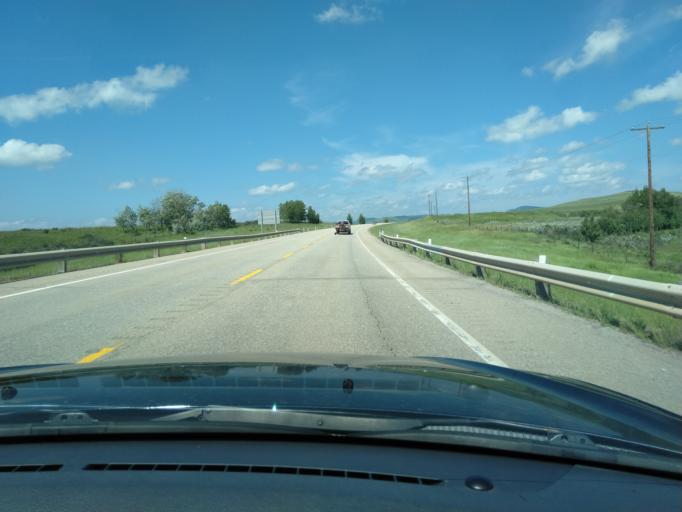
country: CA
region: Alberta
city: Cochrane
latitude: 51.2086
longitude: -114.5202
